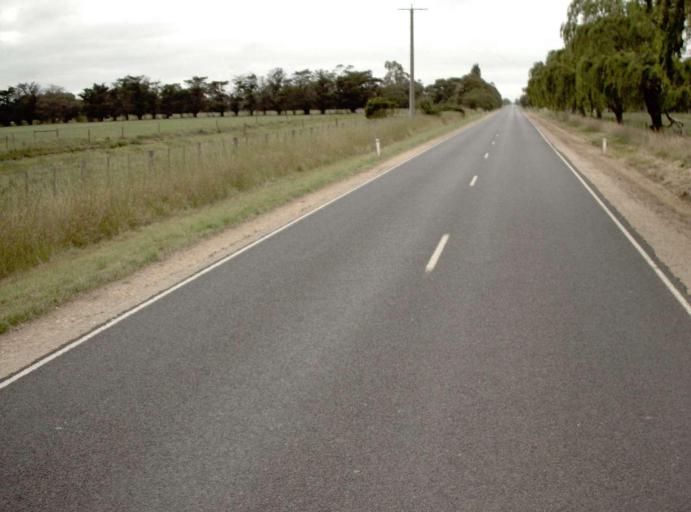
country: AU
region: Victoria
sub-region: Wellington
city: Heyfield
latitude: -38.0266
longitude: 146.8839
